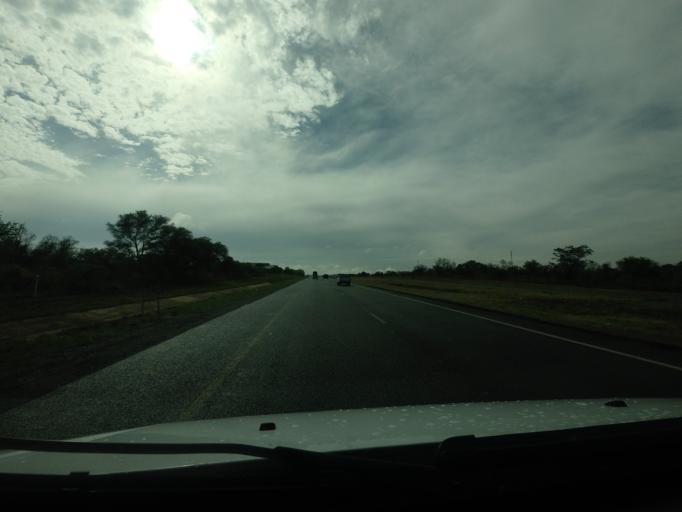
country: ZA
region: Gauteng
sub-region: City of Tshwane Metropolitan Municipality
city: Cullinan
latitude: -25.7698
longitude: 28.4127
